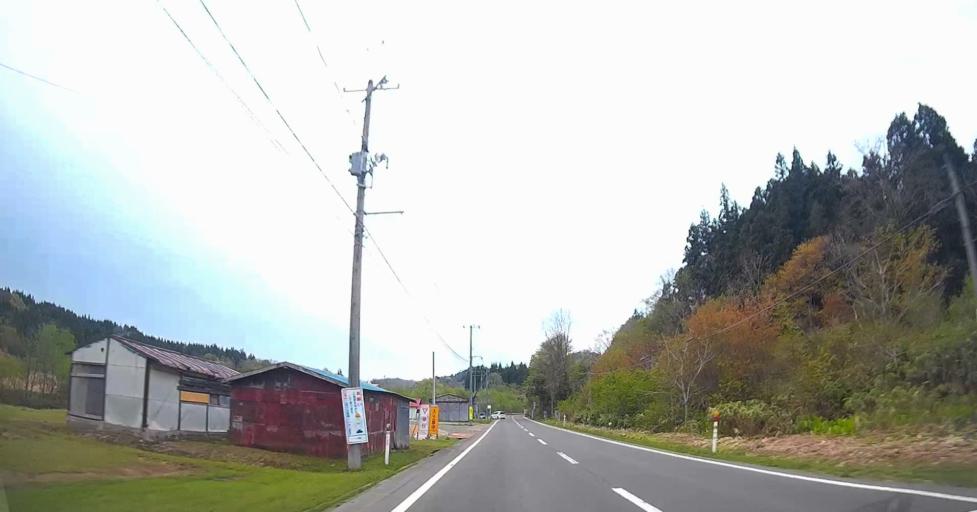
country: JP
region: Aomori
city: Goshogawara
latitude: 41.1299
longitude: 140.5197
